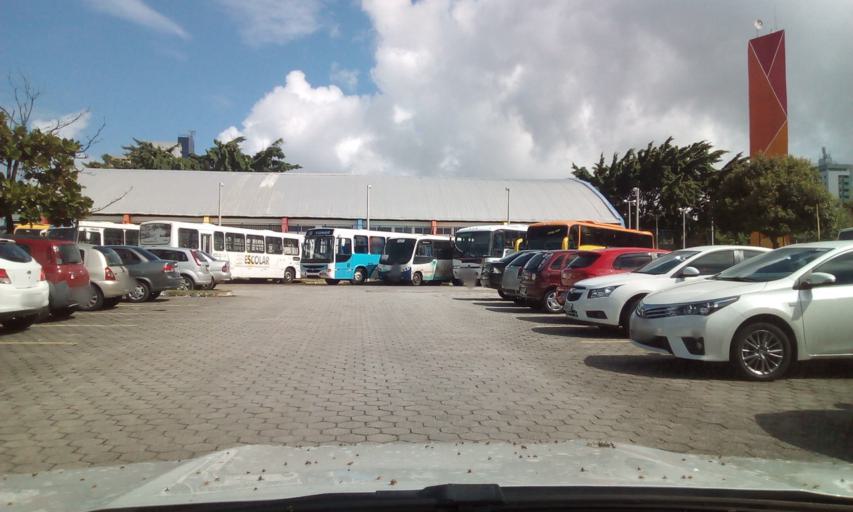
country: BR
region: Paraiba
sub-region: Joao Pessoa
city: Joao Pessoa
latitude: -7.1160
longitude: -34.8441
